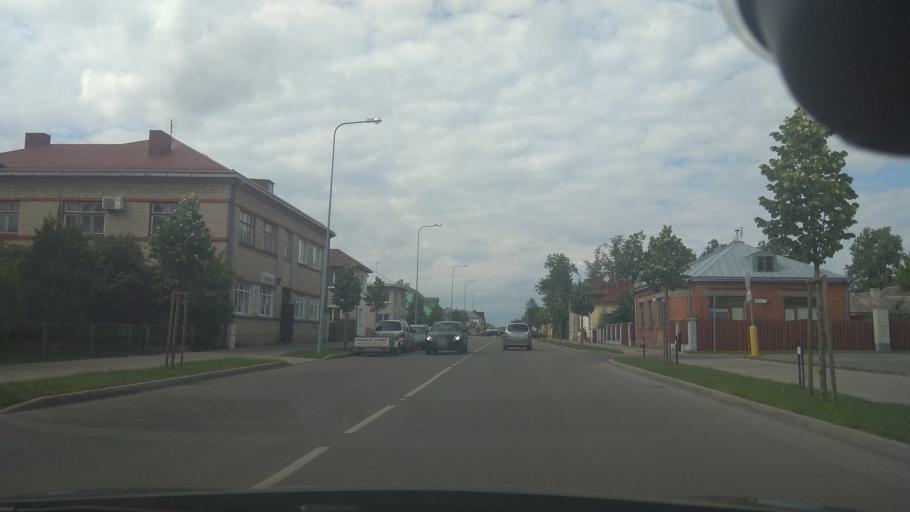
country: LT
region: Marijampoles apskritis
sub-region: Marijampole Municipality
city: Marijampole
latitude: 54.5518
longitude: 23.3535
